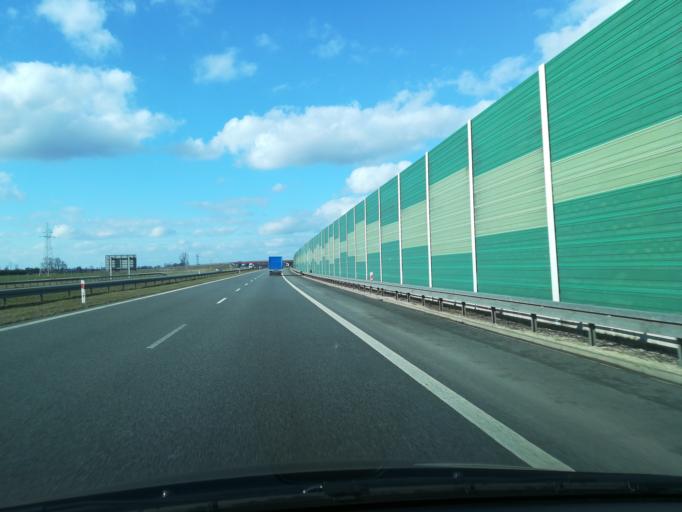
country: PL
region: Lodz Voivodeship
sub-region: Powiat kutnowski
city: Krzyzanow
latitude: 52.2384
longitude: 19.4524
